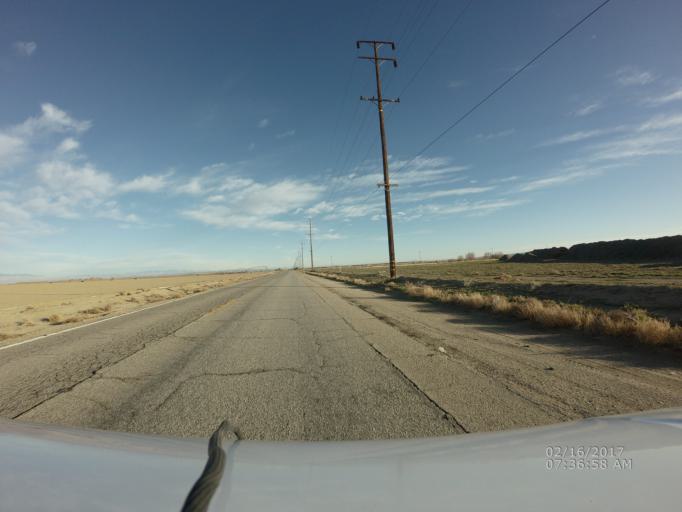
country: US
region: California
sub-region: Los Angeles County
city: Littlerock
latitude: 34.6624
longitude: -117.9697
